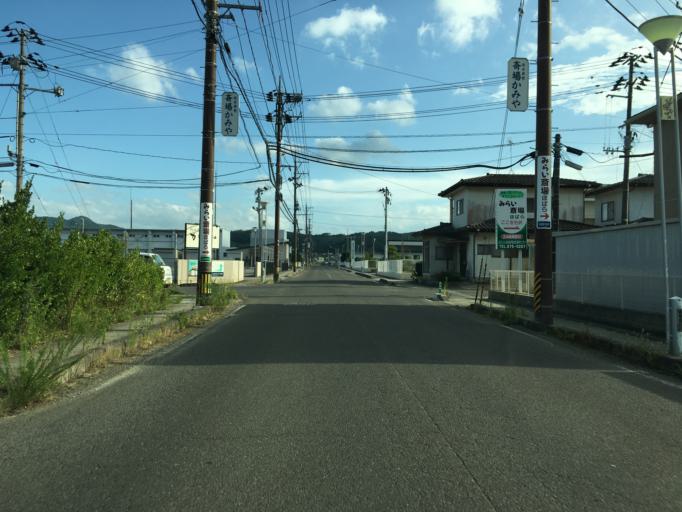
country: JP
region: Fukushima
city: Hobaramachi
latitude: 37.8111
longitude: 140.5517
